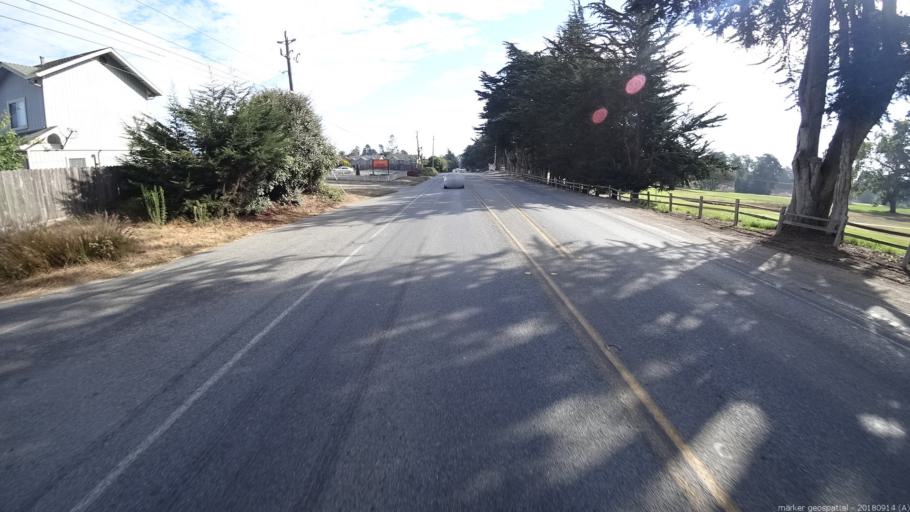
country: US
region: California
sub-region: Monterey County
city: Las Lomas
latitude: 36.8749
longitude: -121.7589
